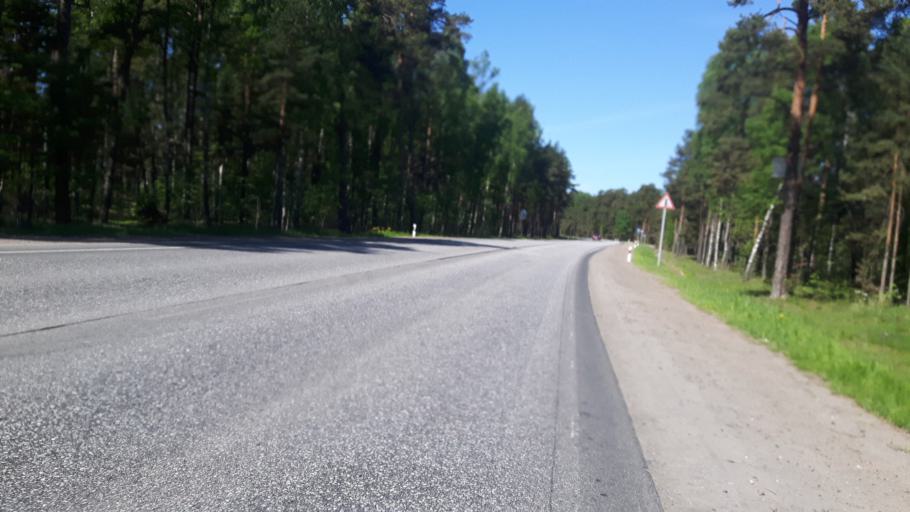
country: RU
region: Leningrad
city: Lebyazh'ye
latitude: 59.9565
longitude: 29.4687
